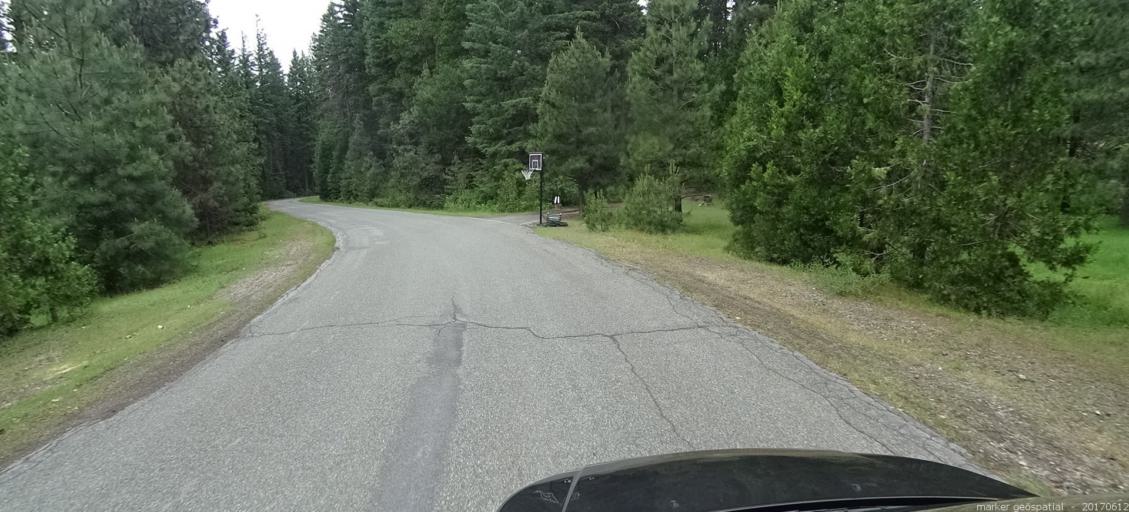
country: US
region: California
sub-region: Siskiyou County
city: Weed
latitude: 41.3652
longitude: -122.3860
